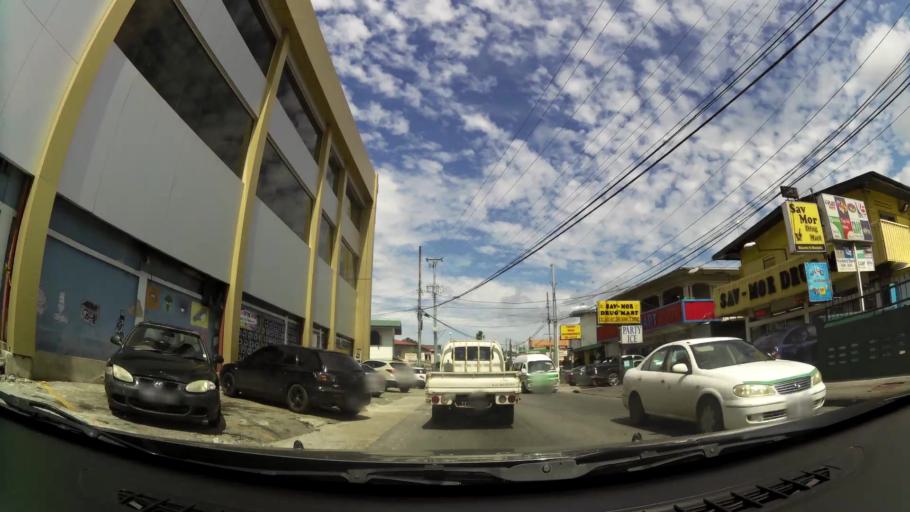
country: TT
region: City of San Fernando
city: Marabella
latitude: 10.2936
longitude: -61.4549
